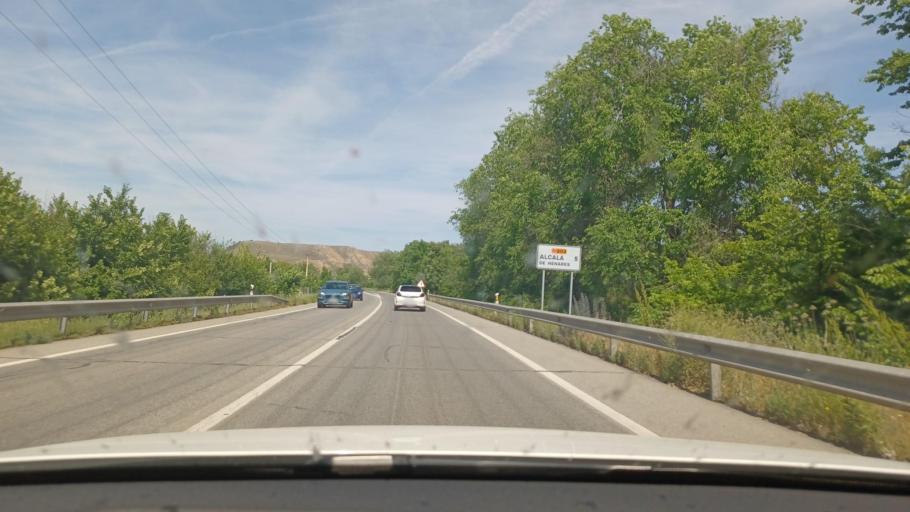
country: ES
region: Madrid
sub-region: Provincia de Madrid
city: Torrejon de Ardoz
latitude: 40.4316
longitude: -3.4422
